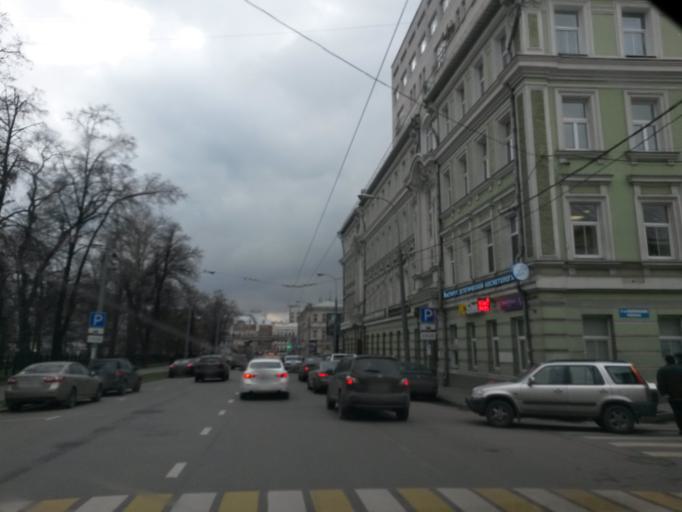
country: RU
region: Moscow
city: Moscow
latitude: 55.7757
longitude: 37.6187
